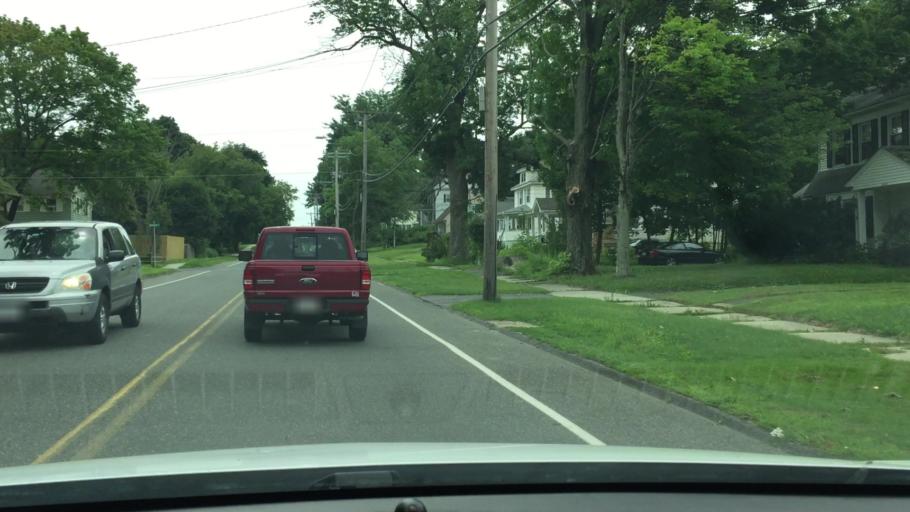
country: US
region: Massachusetts
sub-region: Berkshire County
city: Pittsfield
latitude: 42.4405
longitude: -73.2355
